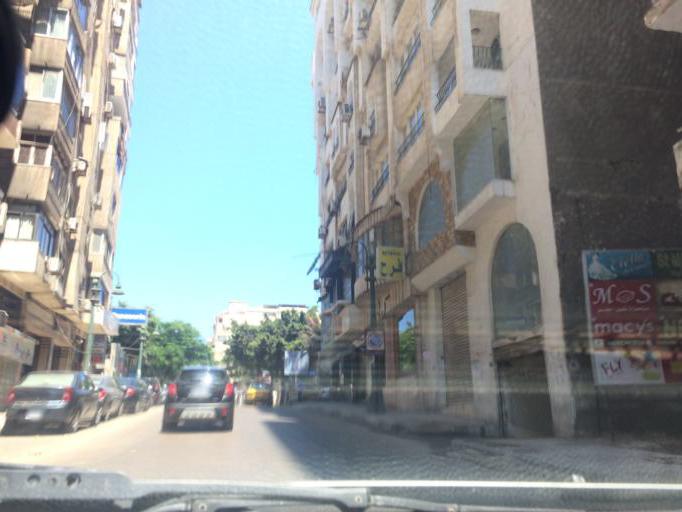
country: EG
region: Alexandria
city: Alexandria
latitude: 31.2308
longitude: 29.9492
